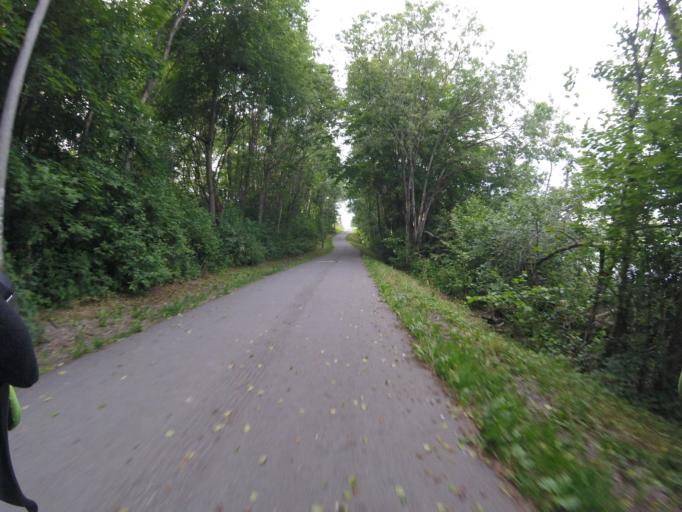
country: NO
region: Akershus
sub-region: Skedsmo
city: Lillestrom
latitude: 59.9698
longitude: 11.0124
